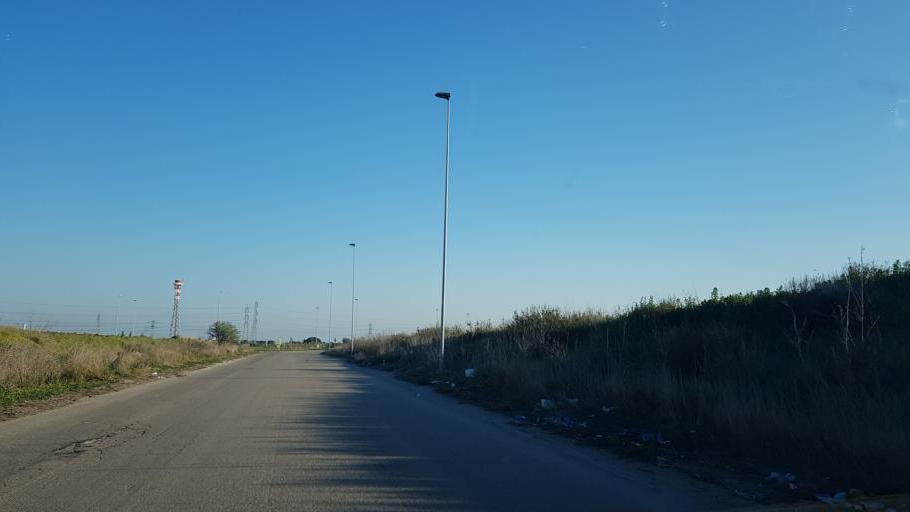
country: IT
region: Apulia
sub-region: Provincia di Brindisi
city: La Rosa
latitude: 40.6199
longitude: 17.9709
